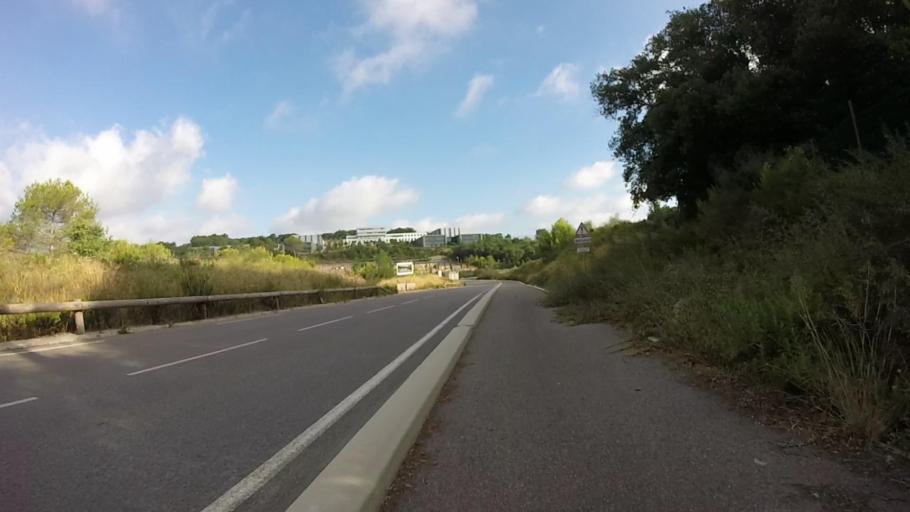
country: FR
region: Provence-Alpes-Cote d'Azur
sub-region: Departement des Alpes-Maritimes
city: Biot
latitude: 43.6129
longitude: 7.0744
